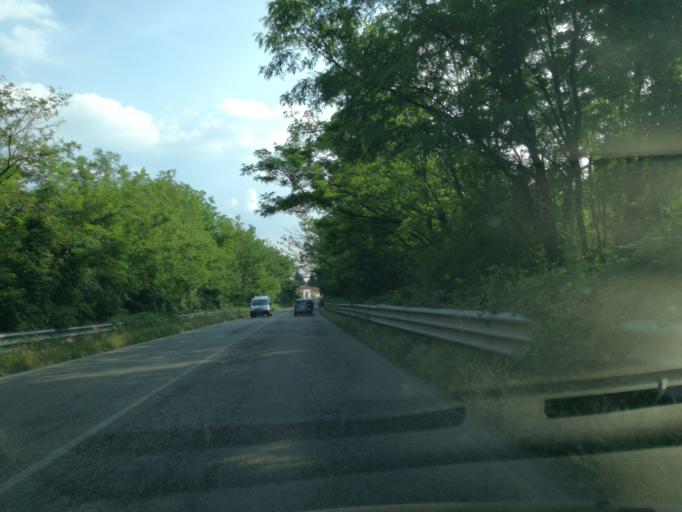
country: IT
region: Lombardy
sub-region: Provincia di Lecco
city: Lomagna
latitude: 45.6616
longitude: 9.3826
